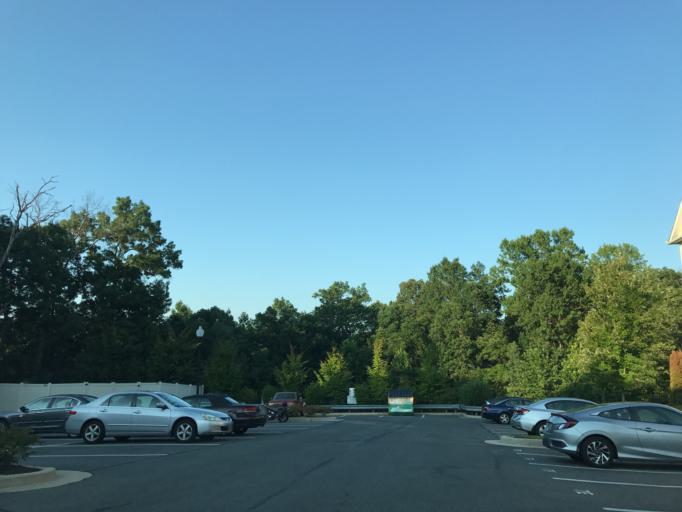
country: US
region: Maryland
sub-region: Baltimore County
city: White Marsh
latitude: 39.3882
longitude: -76.4489
